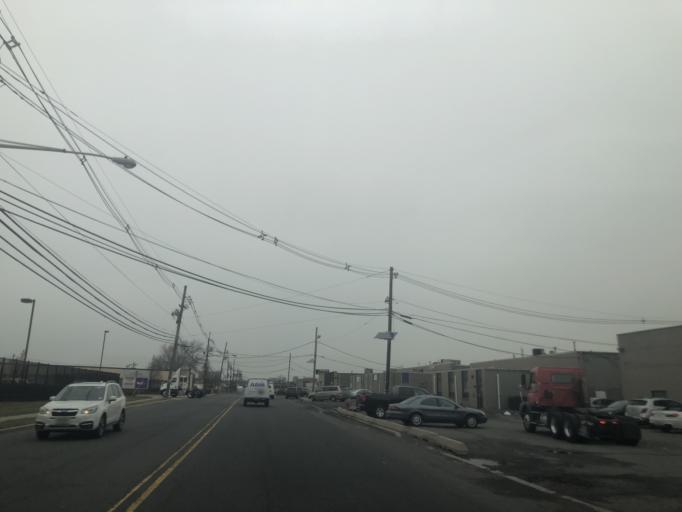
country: US
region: New Jersey
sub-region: Union County
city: Elizabeth
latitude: 40.6687
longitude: -74.1884
